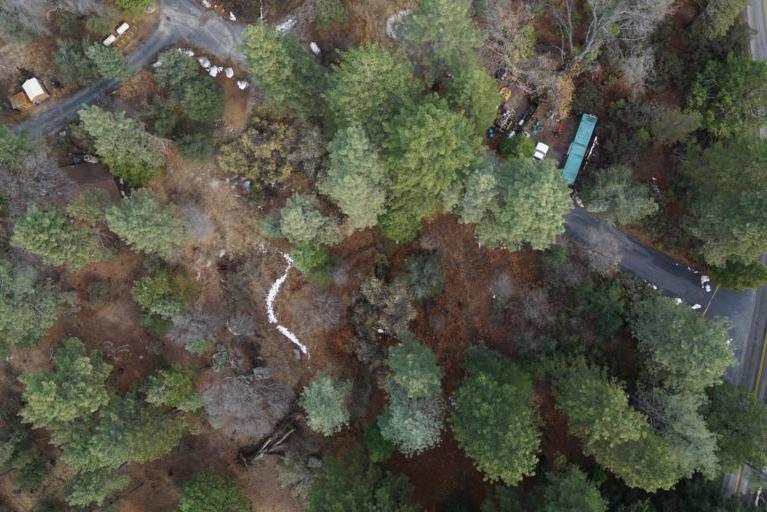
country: US
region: California
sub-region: Riverside County
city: Idyllwild
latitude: 33.7296
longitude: -116.7148
